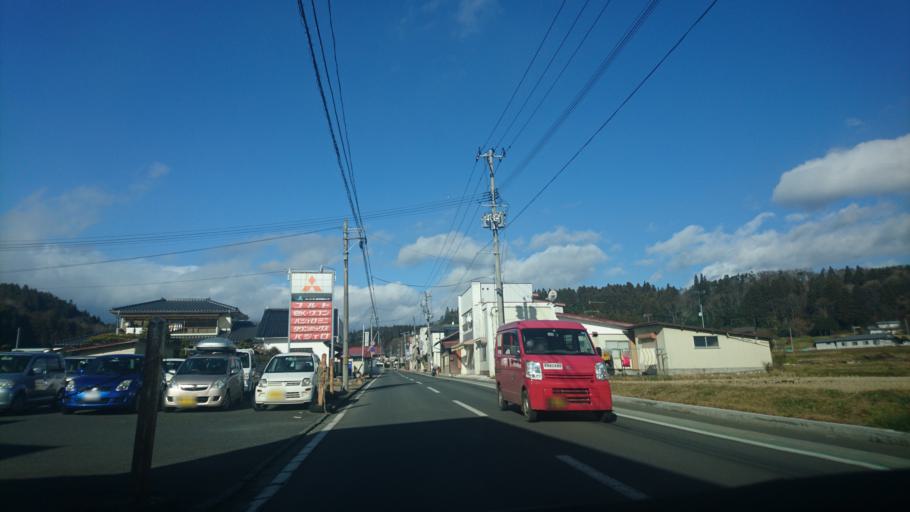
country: JP
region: Iwate
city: Mizusawa
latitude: 39.0513
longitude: 141.3666
